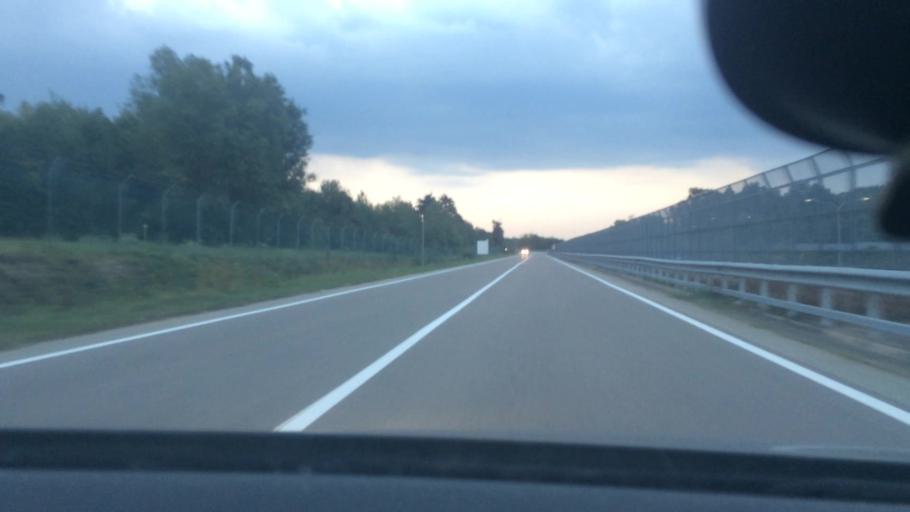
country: IT
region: Lombardy
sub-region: Provincia di Varese
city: Vizzola Ticino
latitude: 45.6178
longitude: 8.7085
